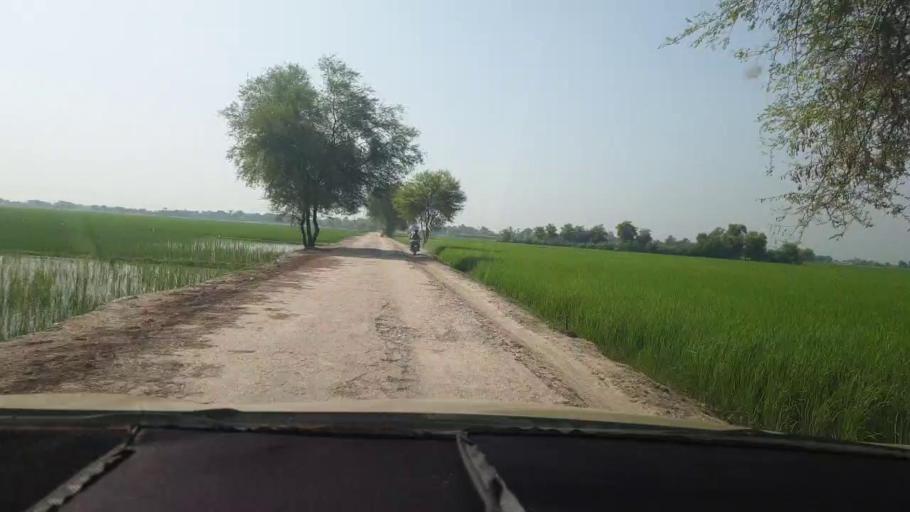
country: PK
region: Sindh
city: Kambar
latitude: 27.5648
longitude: 68.0575
